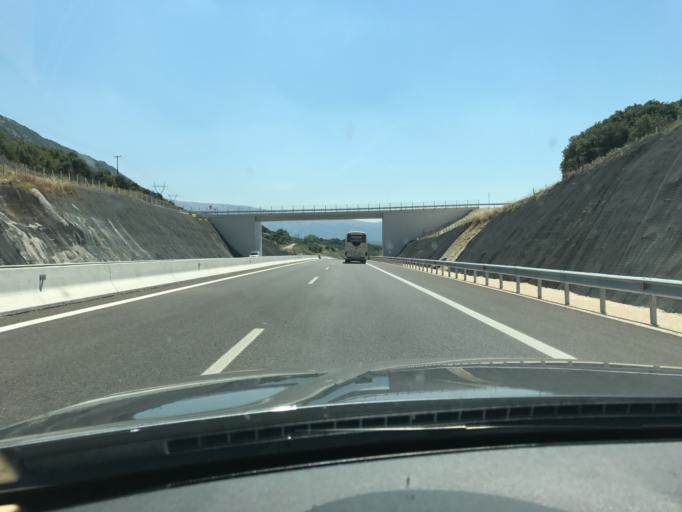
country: GR
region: Epirus
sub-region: Nomos Ioanninon
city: Agia Kyriaki
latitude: 39.4902
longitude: 20.8902
